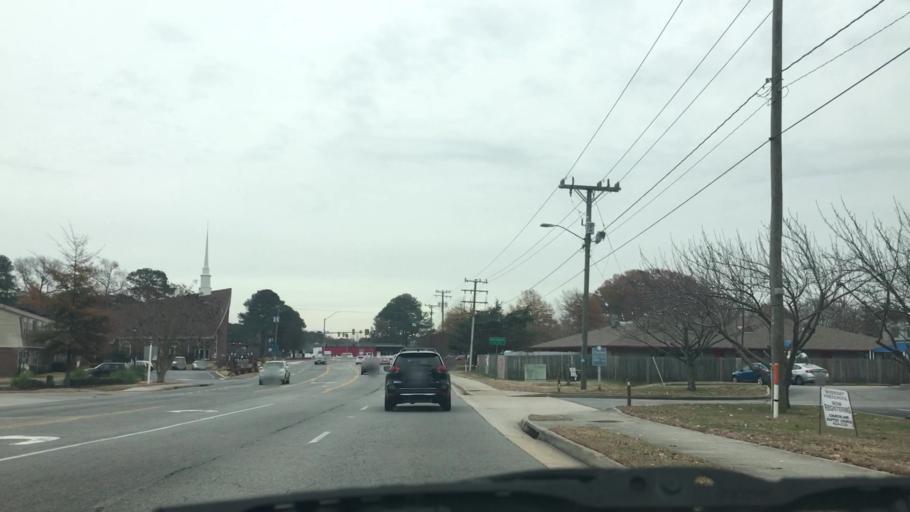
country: US
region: Virginia
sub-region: City of Portsmouth
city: Portsmouth Heights
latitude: 36.8652
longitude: -76.3990
